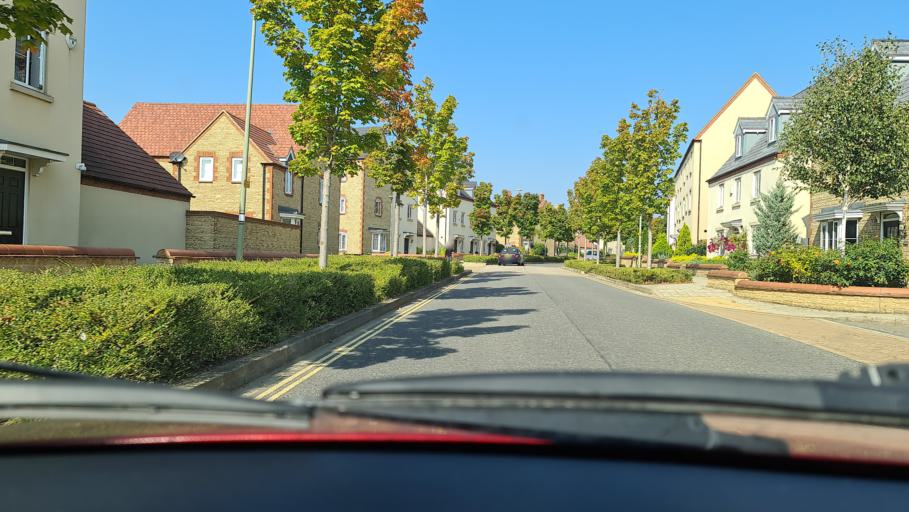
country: GB
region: England
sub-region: Oxfordshire
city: Bicester
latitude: 51.8909
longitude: -1.1700
